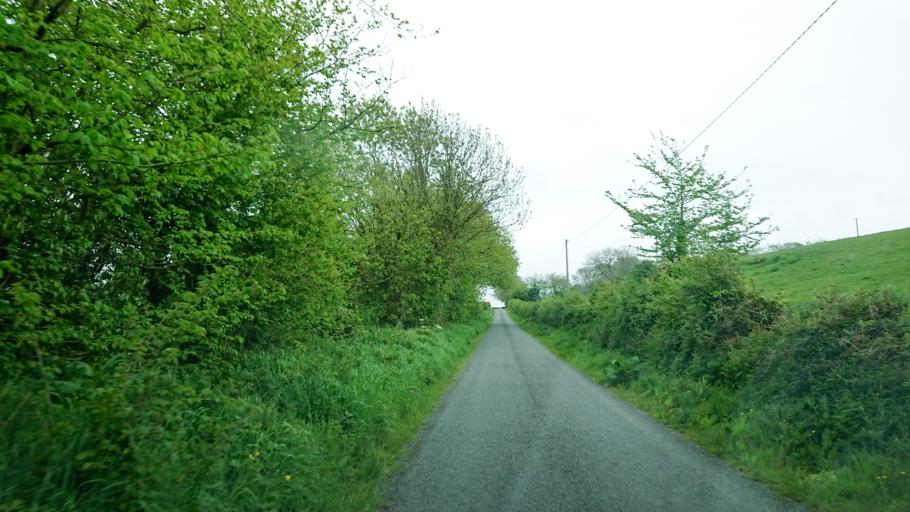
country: IE
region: Munster
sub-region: Waterford
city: Dunmore East
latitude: 52.2220
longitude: -7.0096
